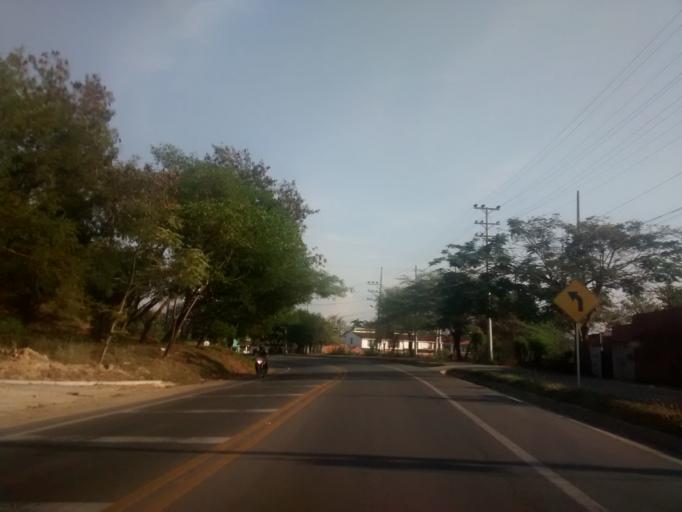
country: CO
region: Cundinamarca
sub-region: Girardot
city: Girardot City
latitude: 4.2971
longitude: -74.7903
